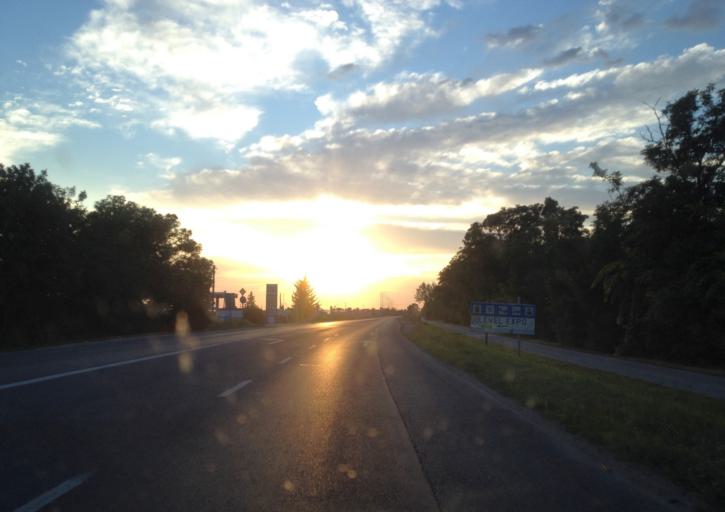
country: HU
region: Gyor-Moson-Sopron
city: Mosonmagyarovar
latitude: 47.8994
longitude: 17.2034
